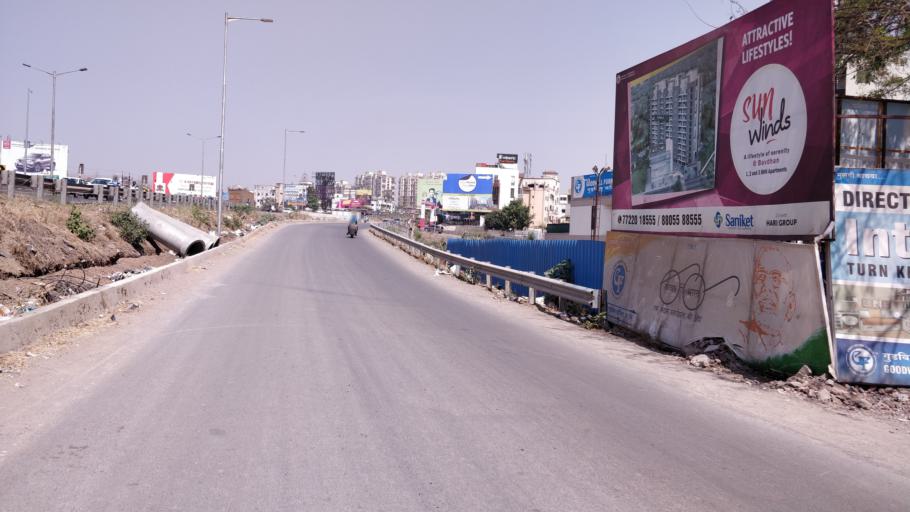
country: IN
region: Maharashtra
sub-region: Pune Division
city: Kharakvasla
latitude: 18.5123
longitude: 73.7709
